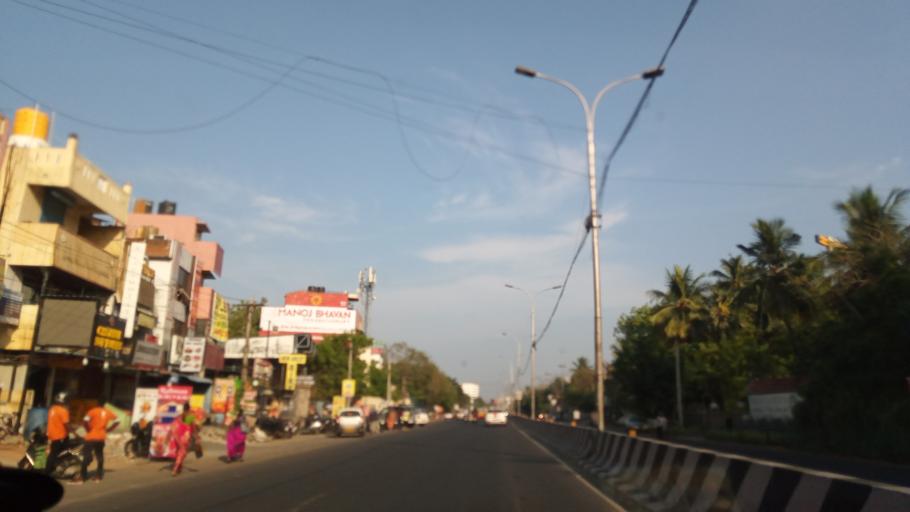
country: IN
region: Tamil Nadu
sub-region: Kancheepuram
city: Manappakkam
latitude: 13.0256
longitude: 80.1755
